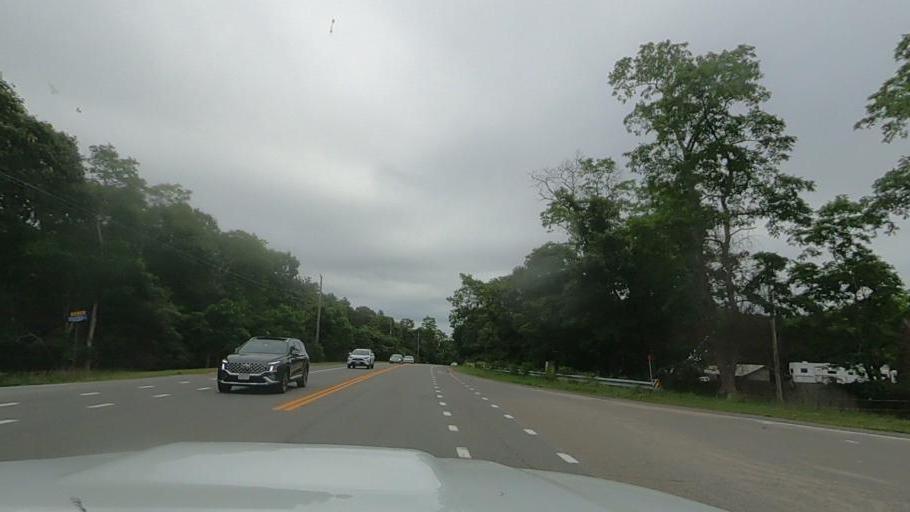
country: US
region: Massachusetts
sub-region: Barnstable County
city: Truro
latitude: 42.0000
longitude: -70.0499
